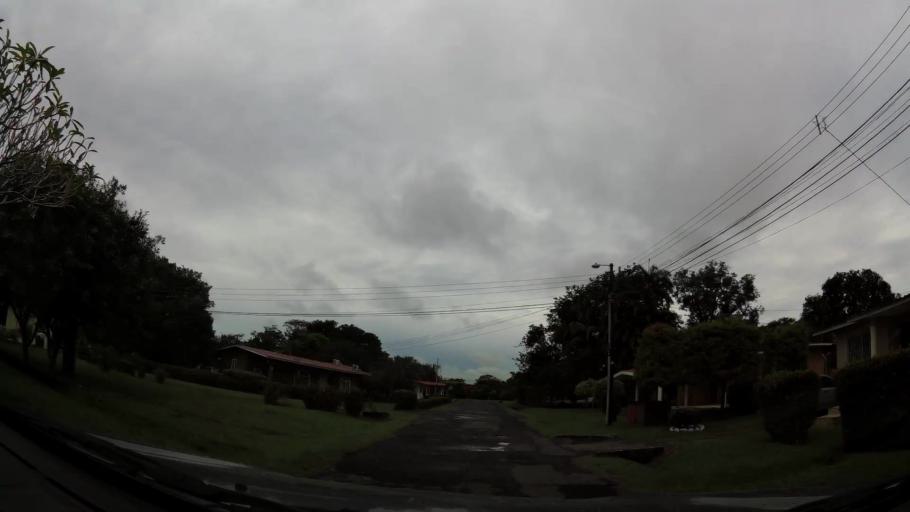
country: PA
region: Chiriqui
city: David
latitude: 8.4239
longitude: -82.4517
